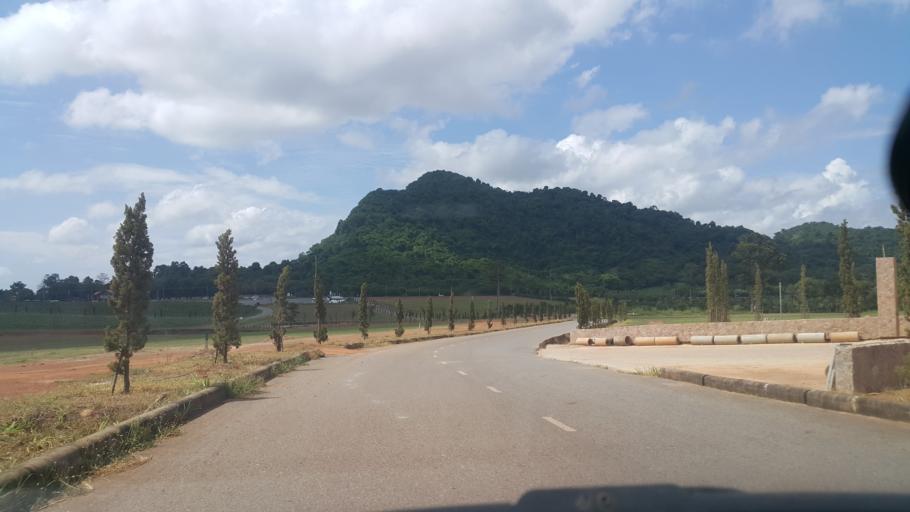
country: TH
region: Rayong
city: Ban Chang
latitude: 12.7547
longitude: 100.9649
